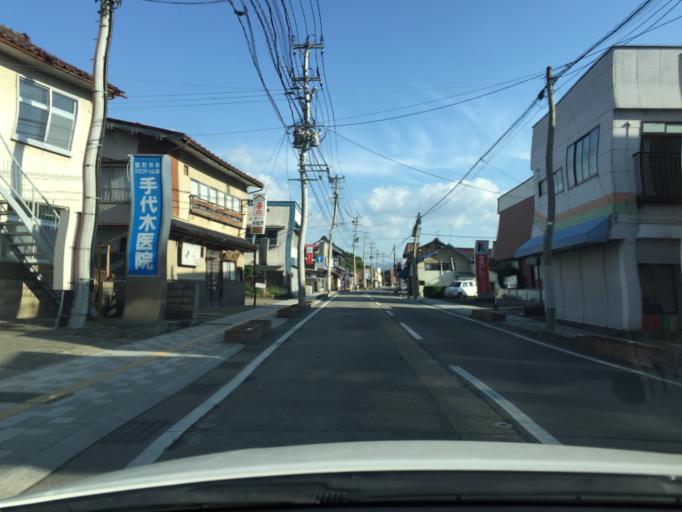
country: JP
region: Fukushima
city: Kitakata
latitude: 37.6554
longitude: 139.8727
